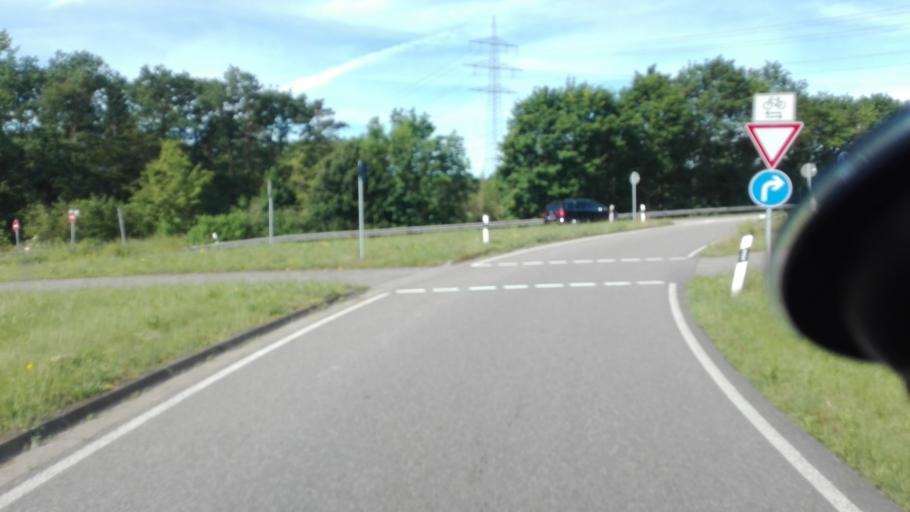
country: DE
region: Baden-Wuerttemberg
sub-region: Karlsruhe Region
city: Eggenstein-Leopoldshafen
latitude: 49.0937
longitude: 8.4142
